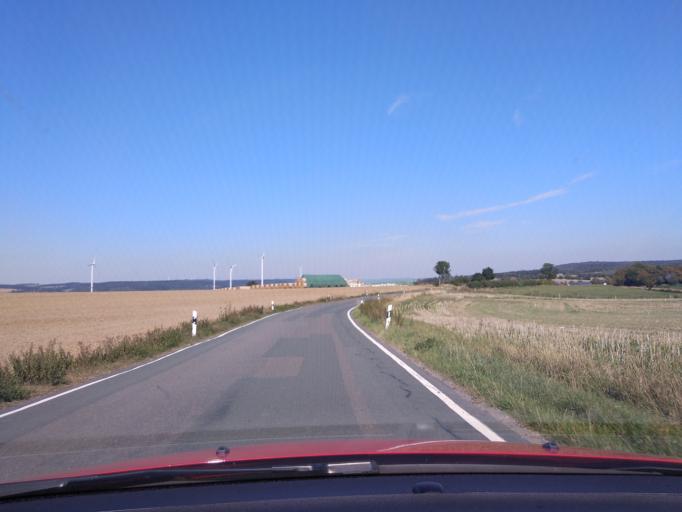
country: DE
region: North Rhine-Westphalia
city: Beverungen
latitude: 51.6771
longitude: 9.3073
